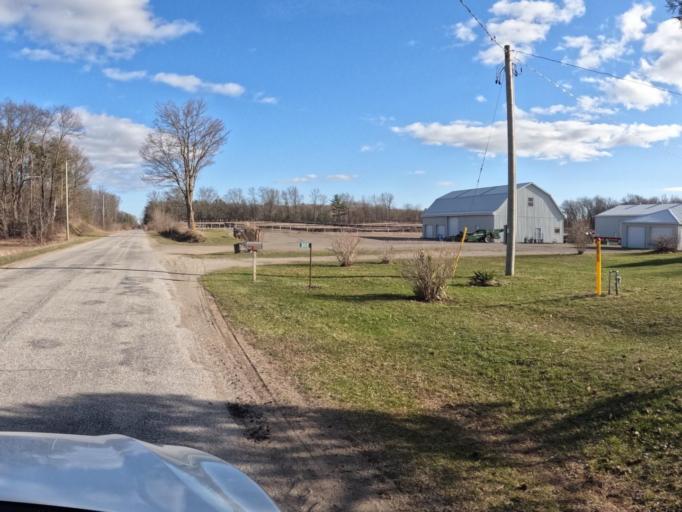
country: CA
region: Ontario
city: Norfolk County
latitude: 42.8147
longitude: -80.5648
